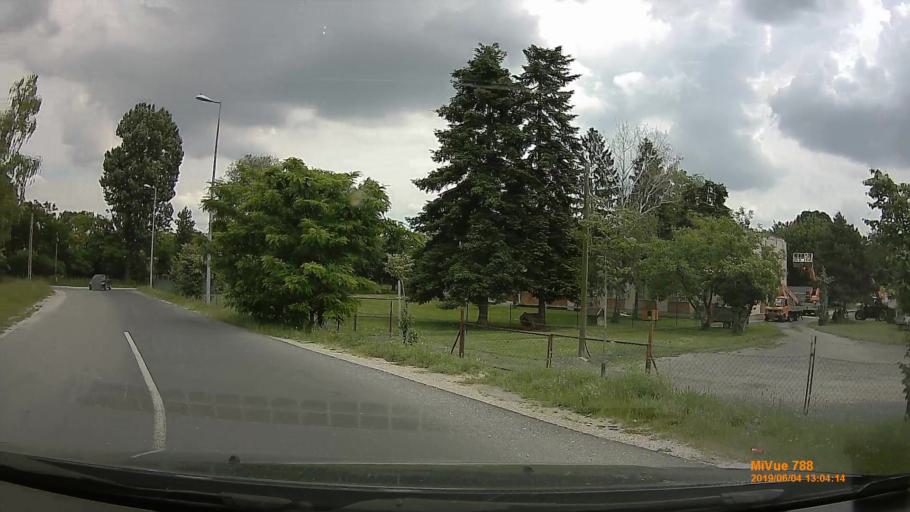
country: HU
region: Budapest
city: Budapest XXII. keruelet
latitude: 47.4006
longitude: 19.0159
